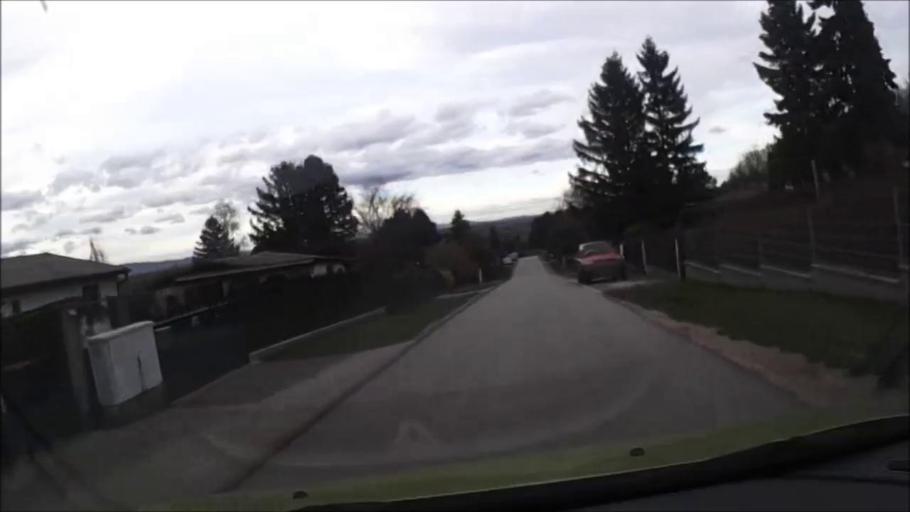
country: AT
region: Burgenland
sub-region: Eisenstadt-Umgebung
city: Loretto
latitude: 47.9041
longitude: 16.5159
